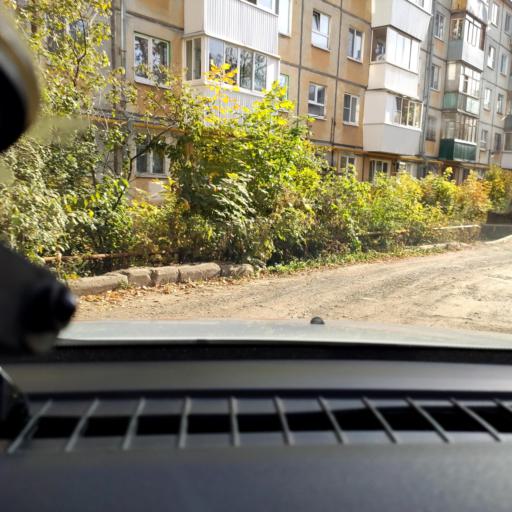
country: RU
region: Samara
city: Samara
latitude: 53.1936
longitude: 50.2095
